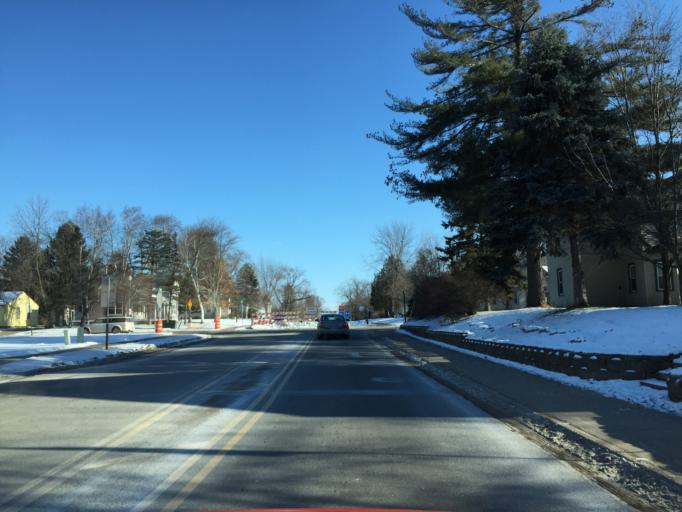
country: US
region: Minnesota
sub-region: Isanti County
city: Cambridge
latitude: 45.5715
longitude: -93.2331
